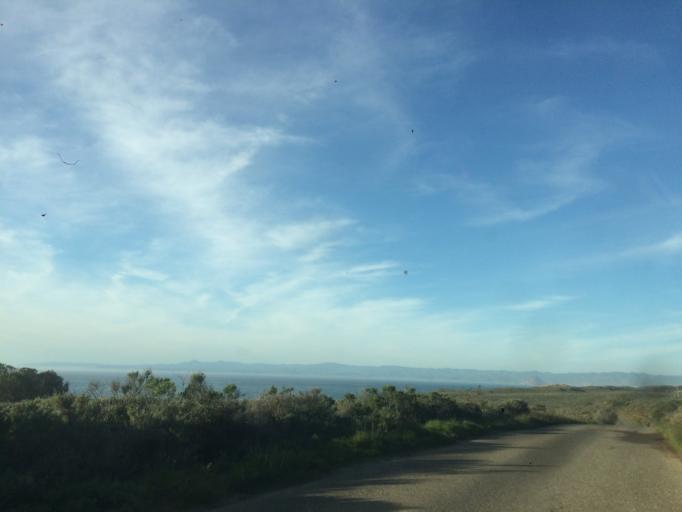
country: US
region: California
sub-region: San Luis Obispo County
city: Los Osos
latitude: 35.2683
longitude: -120.8893
